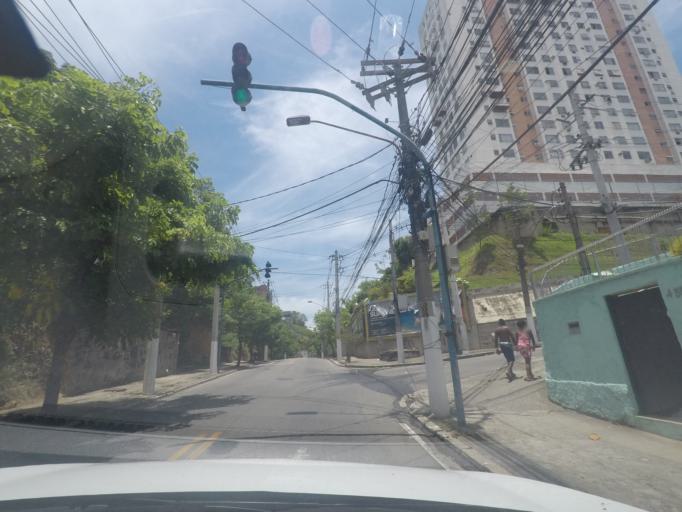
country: BR
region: Rio de Janeiro
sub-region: Niteroi
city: Niteroi
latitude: -22.9000
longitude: -43.1167
